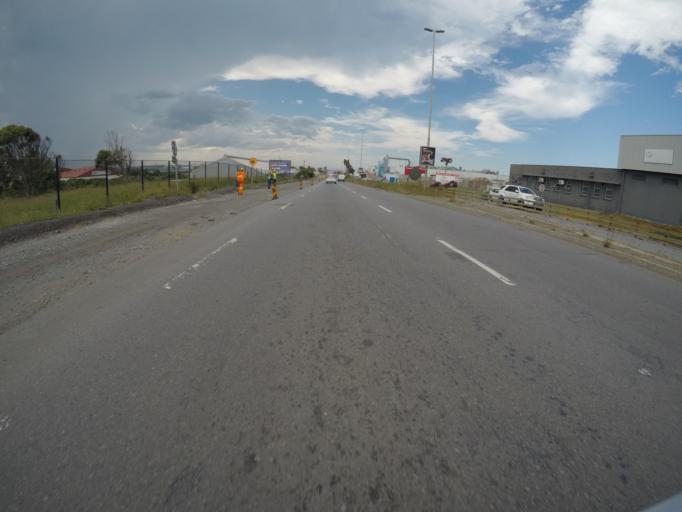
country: ZA
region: Eastern Cape
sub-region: Buffalo City Metropolitan Municipality
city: East London
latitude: -33.0338
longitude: 27.8822
